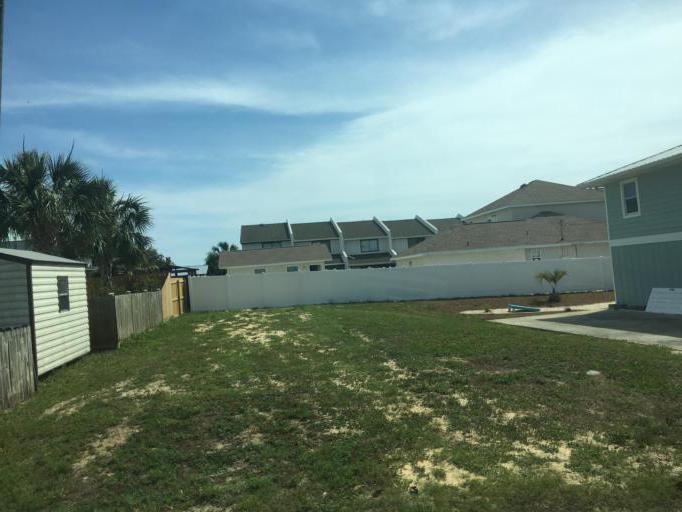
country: US
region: Florida
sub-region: Bay County
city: Laguna Beach
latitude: 30.2472
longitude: -85.9369
